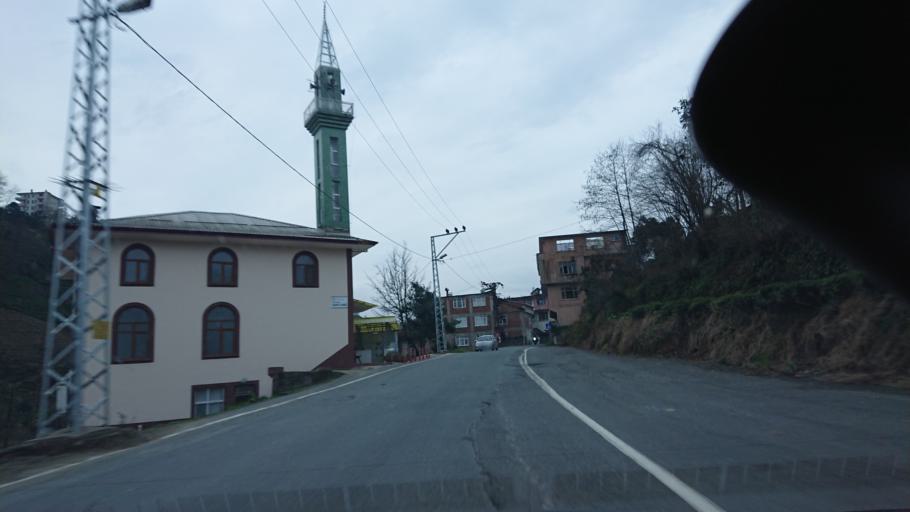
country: TR
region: Rize
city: Rize
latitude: 41.0265
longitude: 40.5055
